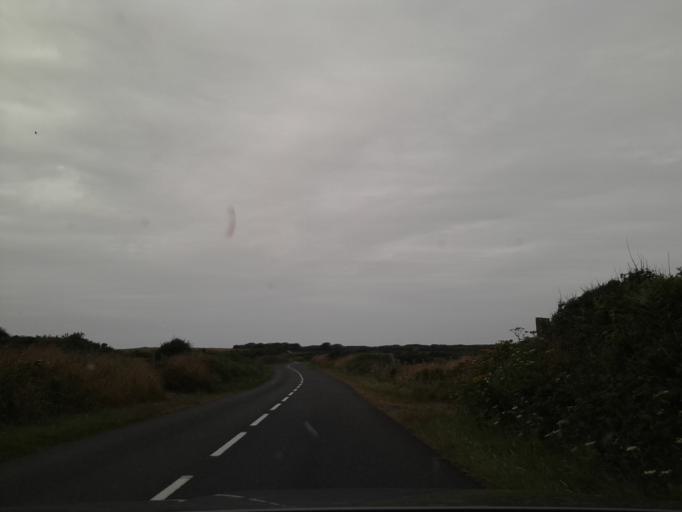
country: FR
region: Lower Normandy
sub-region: Departement de la Manche
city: Beaumont-Hague
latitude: 49.7020
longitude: -1.9287
